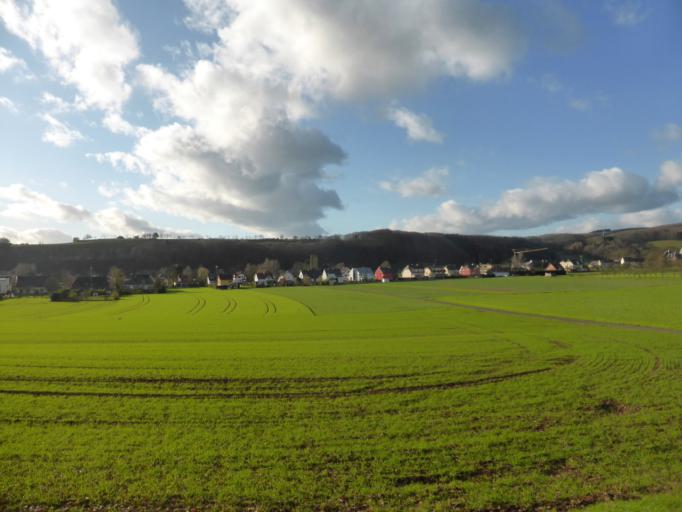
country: LU
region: Diekirch
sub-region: Canton de Diekirch
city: Erpeldange
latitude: 49.8559
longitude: 6.1203
